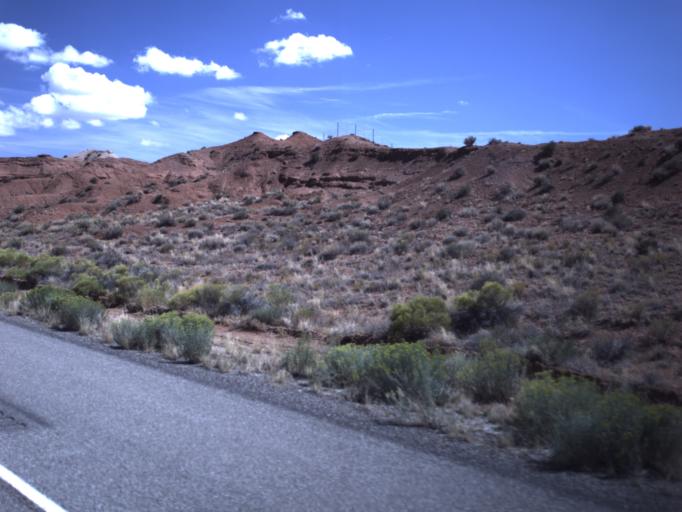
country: US
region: Utah
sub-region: Emery County
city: Ferron
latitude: 38.8463
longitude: -111.0378
